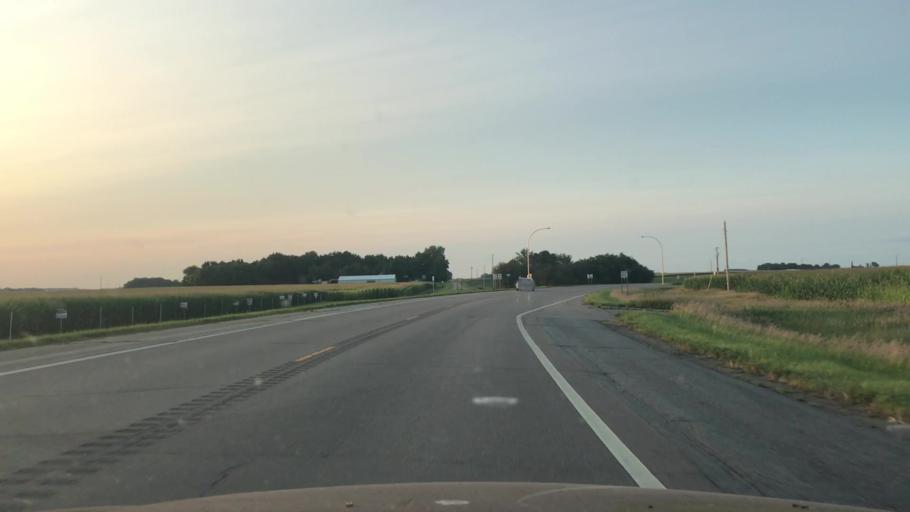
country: US
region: Minnesota
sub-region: Redwood County
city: Redwood Falls
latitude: 44.4113
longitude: -95.1276
